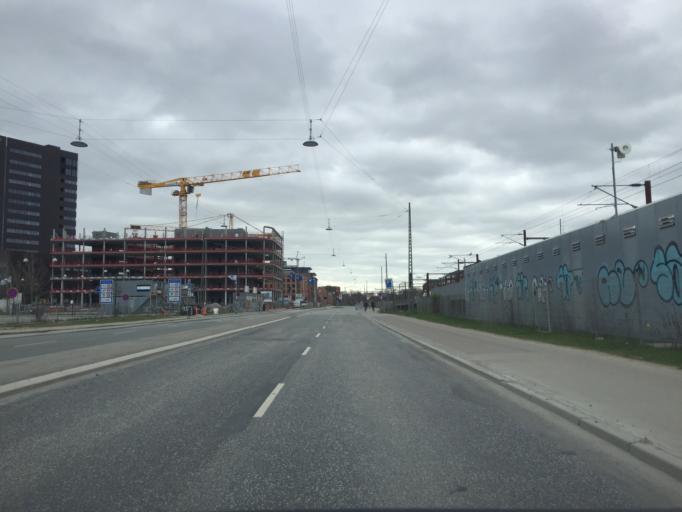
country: DK
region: Capital Region
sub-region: Kobenhavn
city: Christianshavn
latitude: 55.7025
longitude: 12.5922
